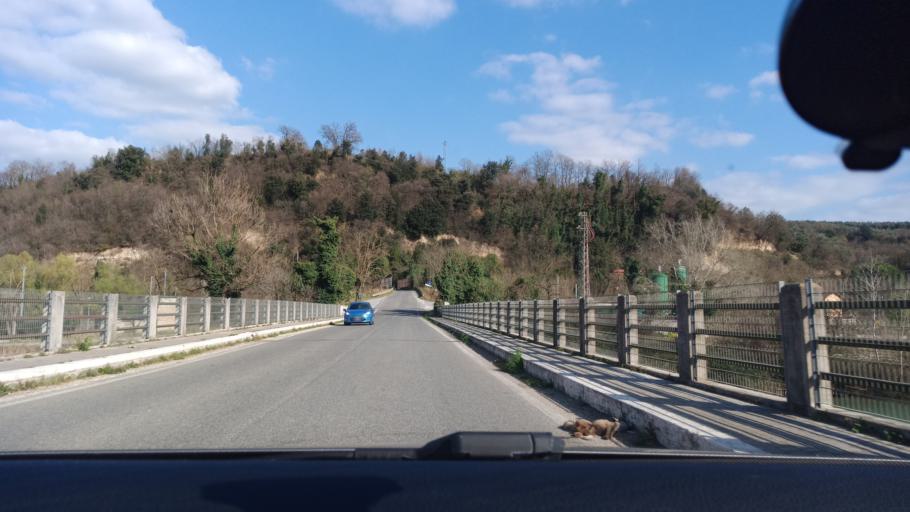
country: IT
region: Latium
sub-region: Citta metropolitana di Roma Capitale
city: Torrita Tiberina
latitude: 42.2354
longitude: 12.6300
